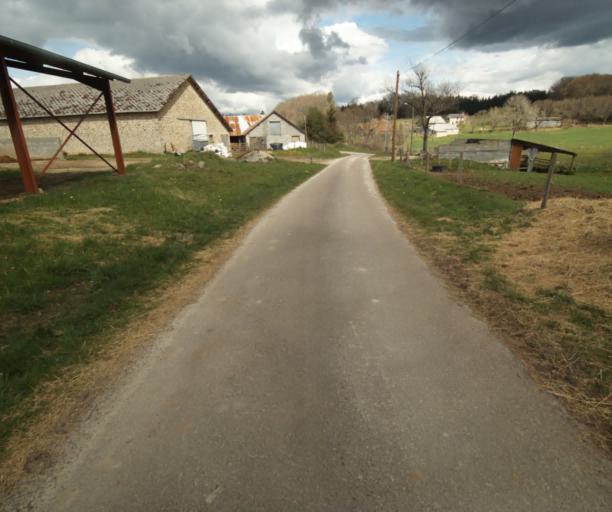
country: FR
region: Limousin
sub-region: Departement de la Correze
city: Correze
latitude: 45.2558
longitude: 1.9031
